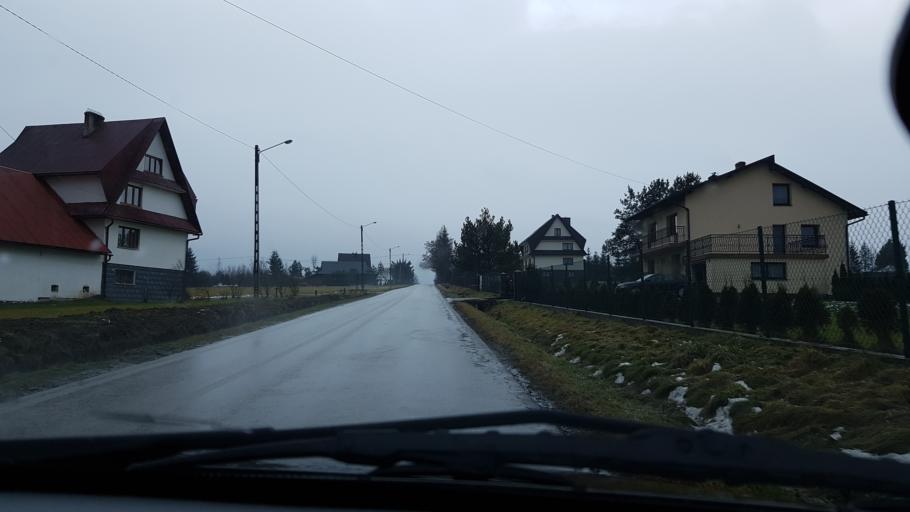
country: PL
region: Lesser Poland Voivodeship
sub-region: Powiat nowotarski
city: Spytkowice
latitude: 49.6018
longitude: 19.8424
